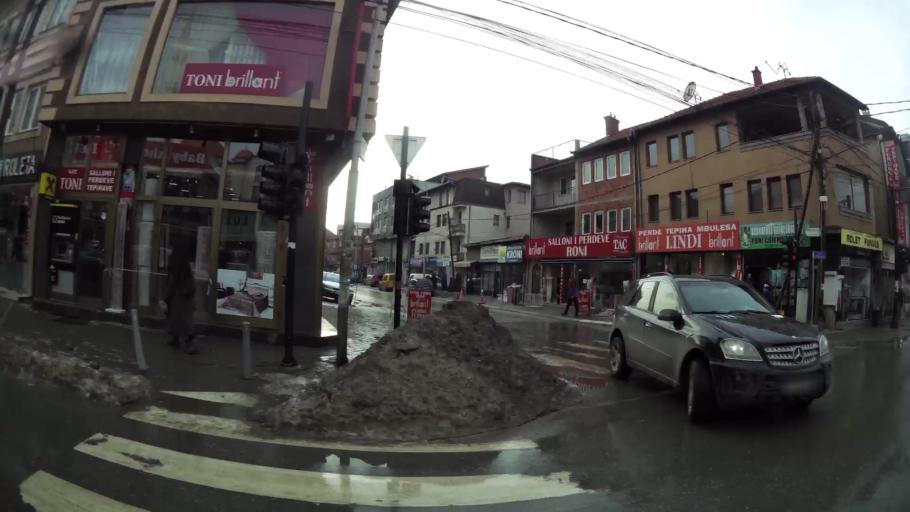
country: XK
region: Pristina
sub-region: Komuna e Prishtines
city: Pristina
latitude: 42.6690
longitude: 21.1638
